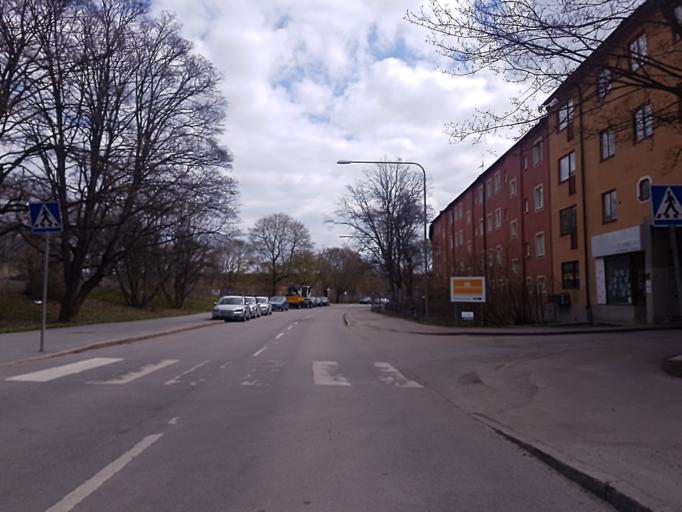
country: SE
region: Stockholm
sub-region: Stockholms Kommun
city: OEstermalm
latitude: 59.2945
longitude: 18.1091
